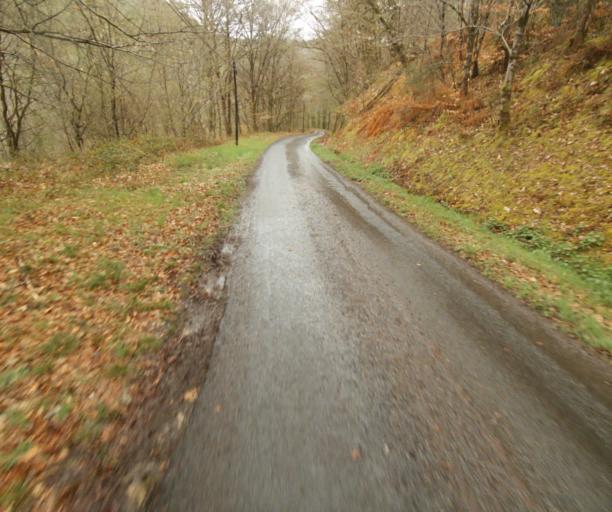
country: FR
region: Limousin
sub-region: Departement de la Correze
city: Saint-Privat
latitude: 45.2202
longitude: 2.0331
